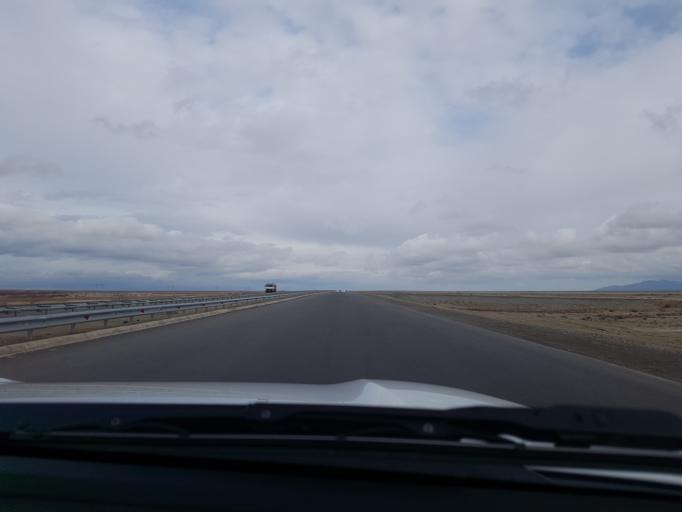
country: TM
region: Balkan
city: Gazanjyk
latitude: 39.2647
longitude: 55.1232
